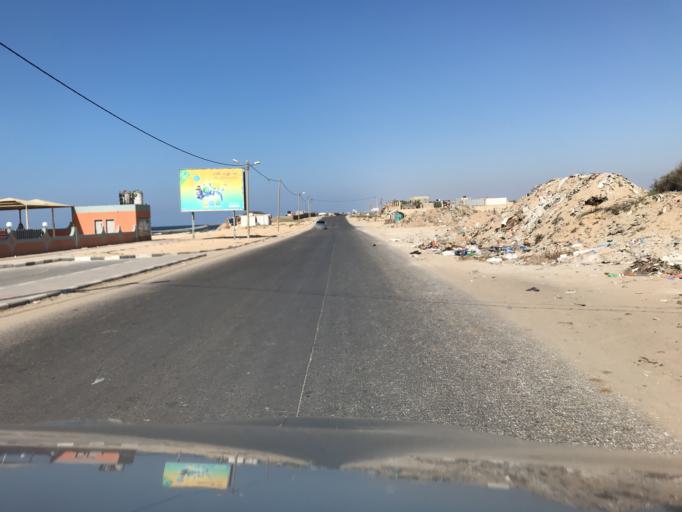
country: PS
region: Gaza Strip
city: Dayr al Balah
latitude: 31.4302
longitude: 34.3437
